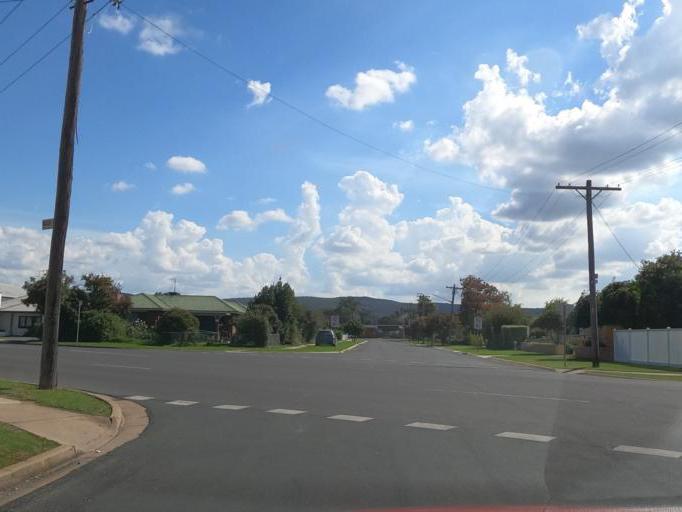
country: AU
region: New South Wales
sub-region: Albury Municipality
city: North Albury
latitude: -36.0559
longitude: 146.9287
